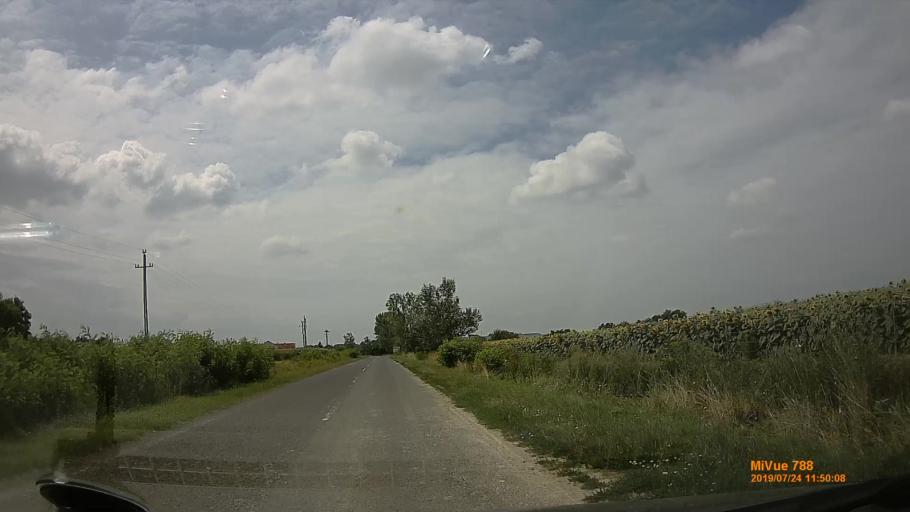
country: UA
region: Zakarpattia
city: Batiovo
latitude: 48.2424
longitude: 22.4405
